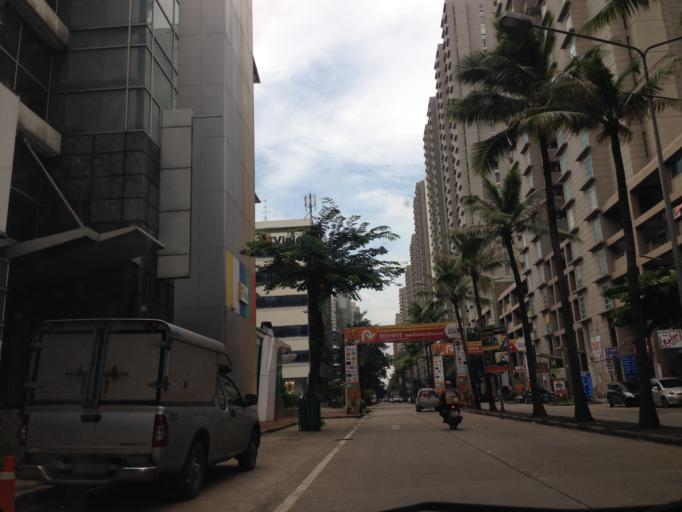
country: TH
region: Nonthaburi
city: Pak Kret
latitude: 13.9221
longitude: 100.5378
